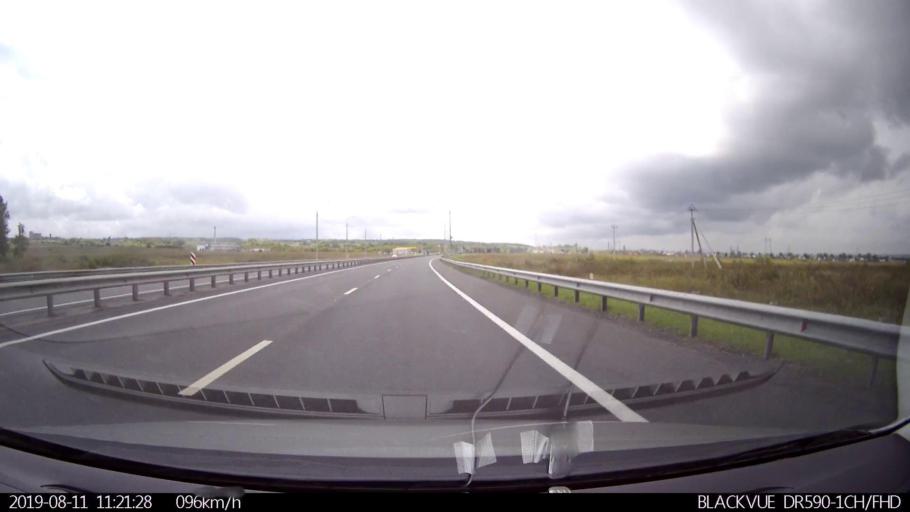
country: RU
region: Ulyanovsk
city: Novoul'yanovsk
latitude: 54.1466
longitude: 48.2632
